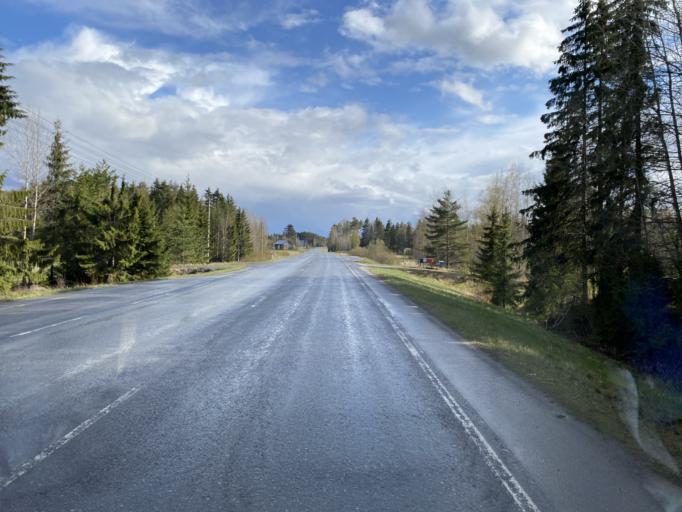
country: FI
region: Pirkanmaa
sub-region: Etelae-Pirkanmaa
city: Viiala
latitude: 61.2140
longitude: 23.7352
